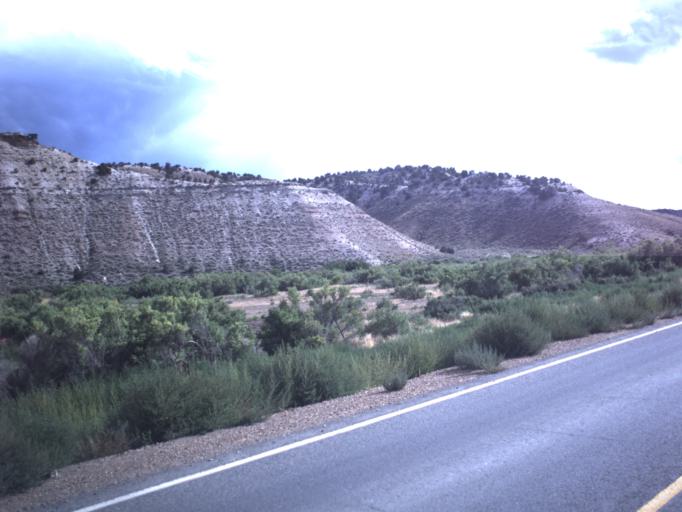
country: US
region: Utah
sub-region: Duchesne County
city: Duchesne
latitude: 40.1271
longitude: -110.4399
